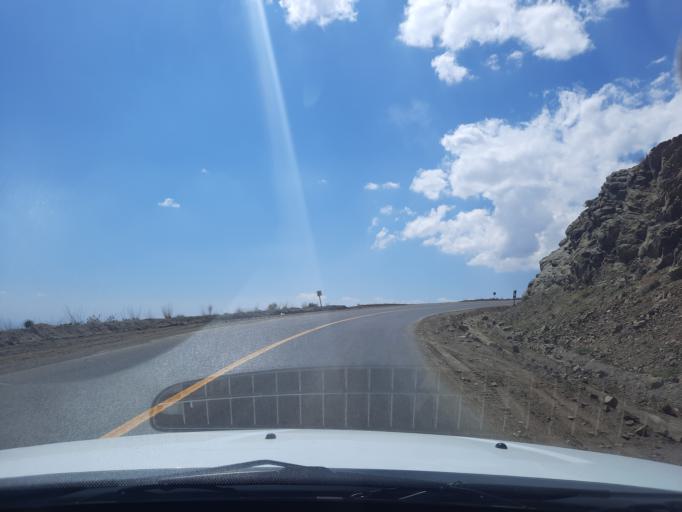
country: IR
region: Qazvin
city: Qazvin
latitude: 36.3772
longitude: 50.2121
